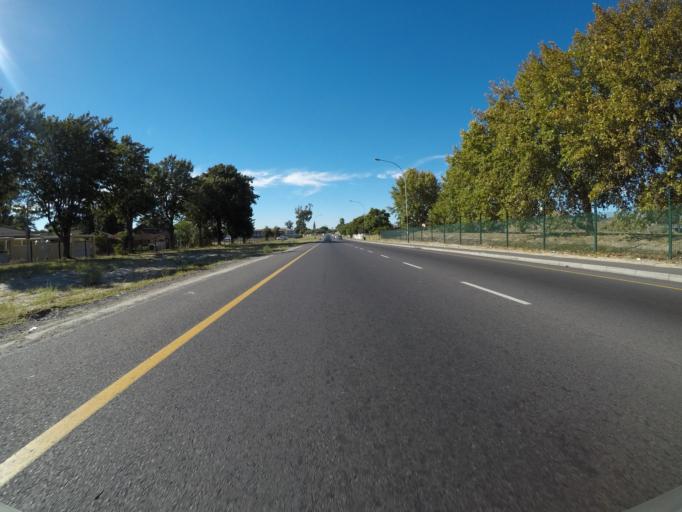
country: ZA
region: Western Cape
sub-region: City of Cape Town
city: Kraaifontein
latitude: -33.9382
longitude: 18.6768
